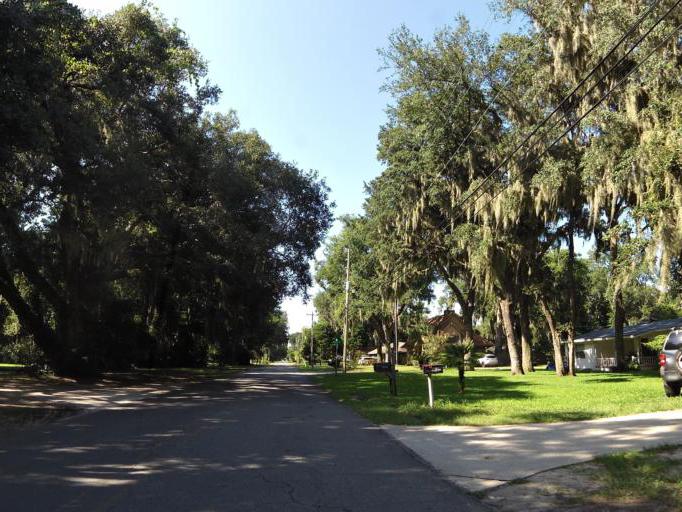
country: US
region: Florida
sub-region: Nassau County
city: Fernandina Beach
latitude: 30.6406
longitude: -81.4629
